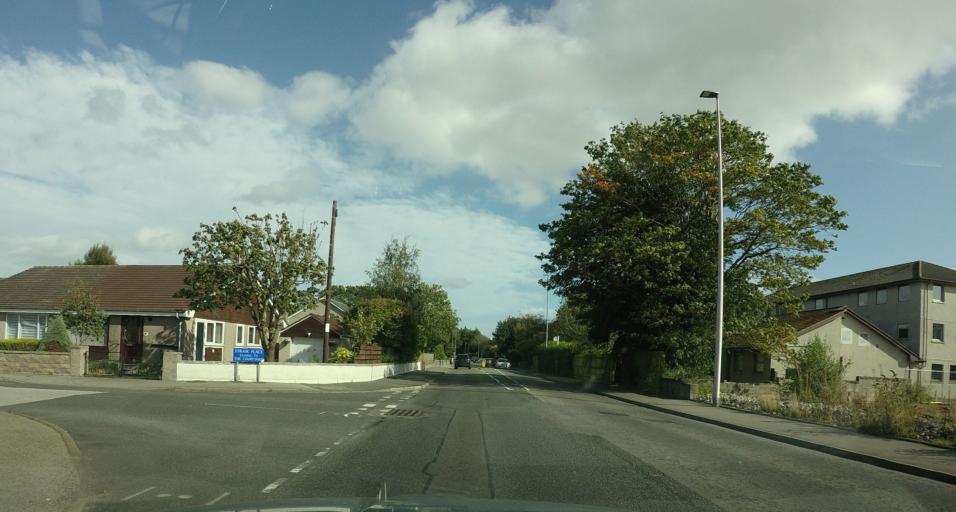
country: GB
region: Scotland
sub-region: Aberdeenshire
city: Westhill
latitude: 57.1496
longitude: -2.2940
